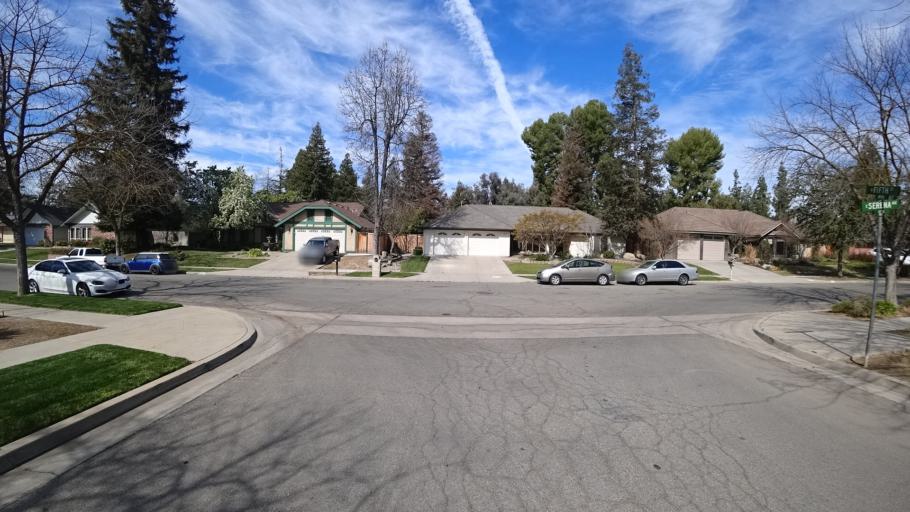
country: US
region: California
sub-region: Fresno County
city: Clovis
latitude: 36.8652
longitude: -119.7681
